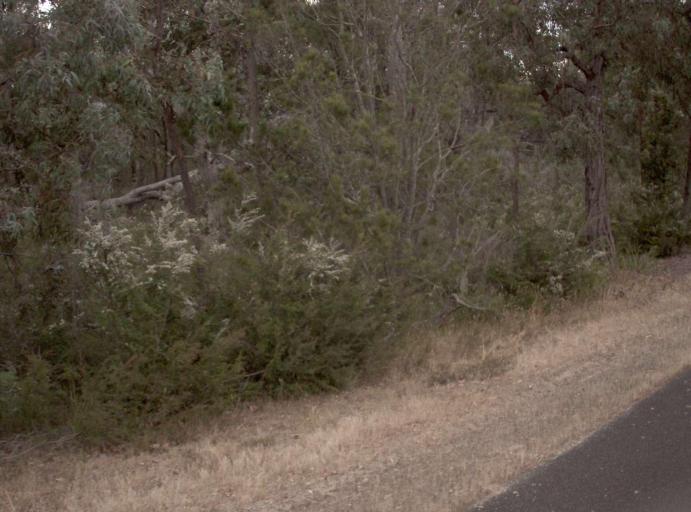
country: AU
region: Victoria
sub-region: Wellington
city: Sale
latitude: -38.3407
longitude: 147.0060
